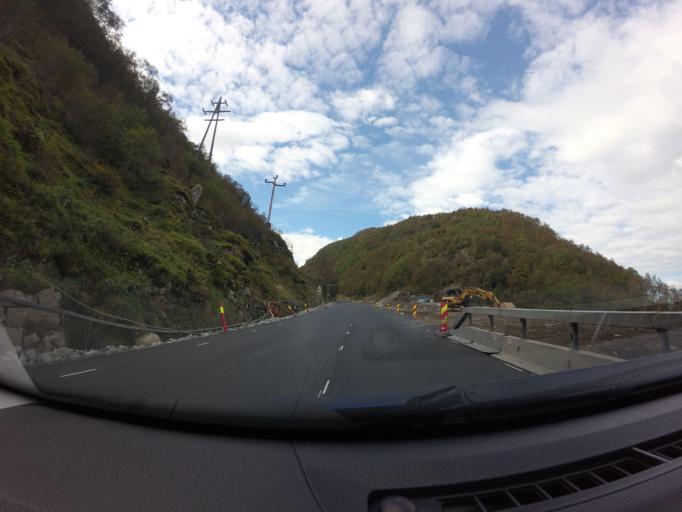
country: NO
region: Rogaland
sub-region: Forsand
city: Forsand
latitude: 58.8392
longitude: 6.1546
